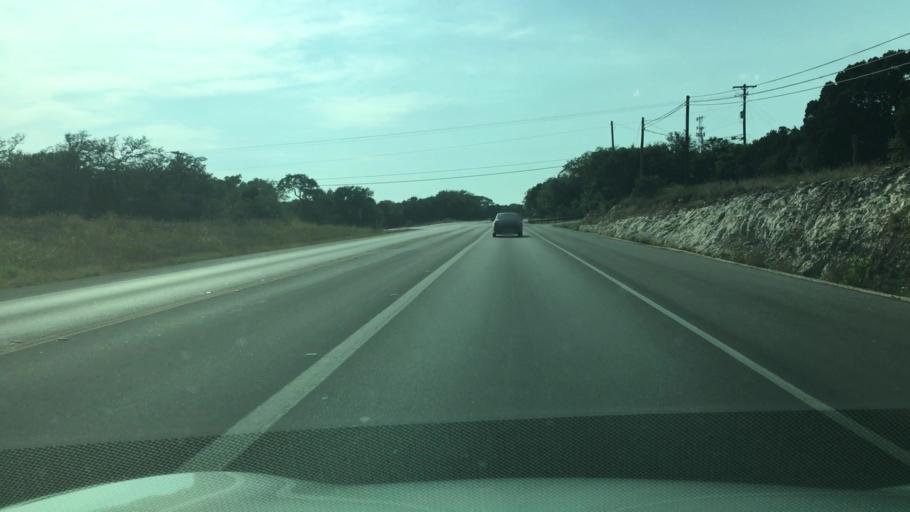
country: US
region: Texas
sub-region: Hays County
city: Wimberley
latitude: 29.9198
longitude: -98.0566
